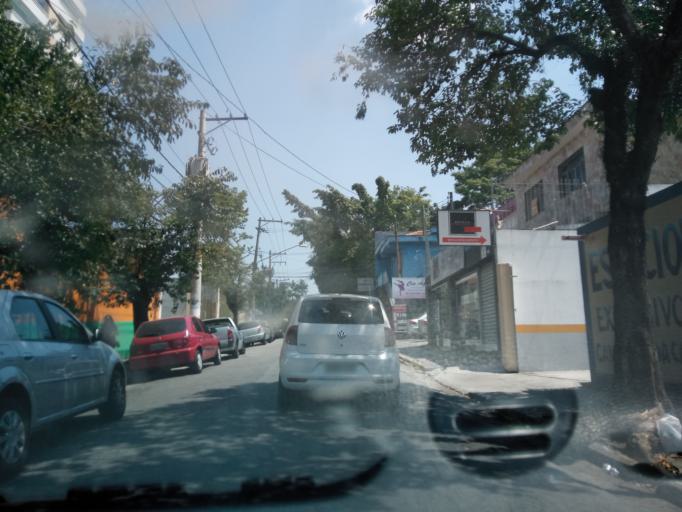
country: BR
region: Sao Paulo
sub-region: Sao Bernardo Do Campo
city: Sao Bernardo do Campo
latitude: -23.7204
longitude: -46.5650
